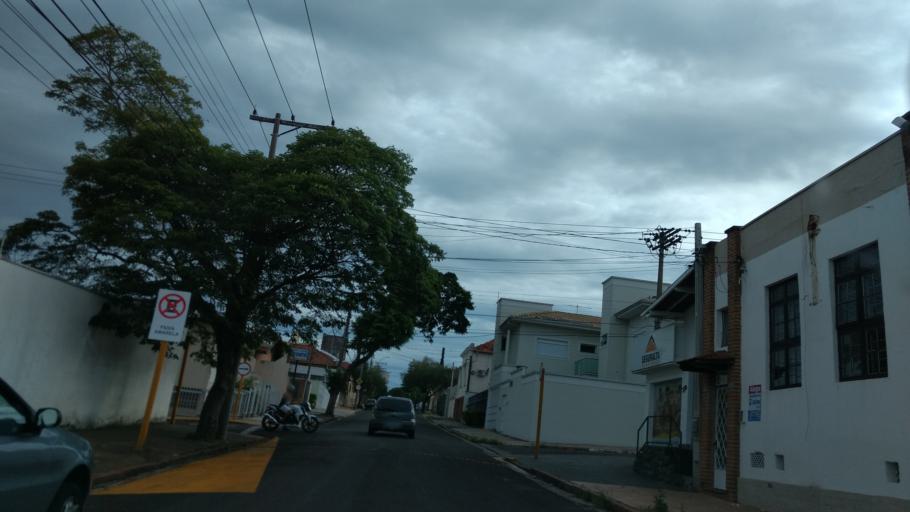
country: BR
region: Sao Paulo
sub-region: Botucatu
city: Botucatu
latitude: -22.8825
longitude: -48.4424
